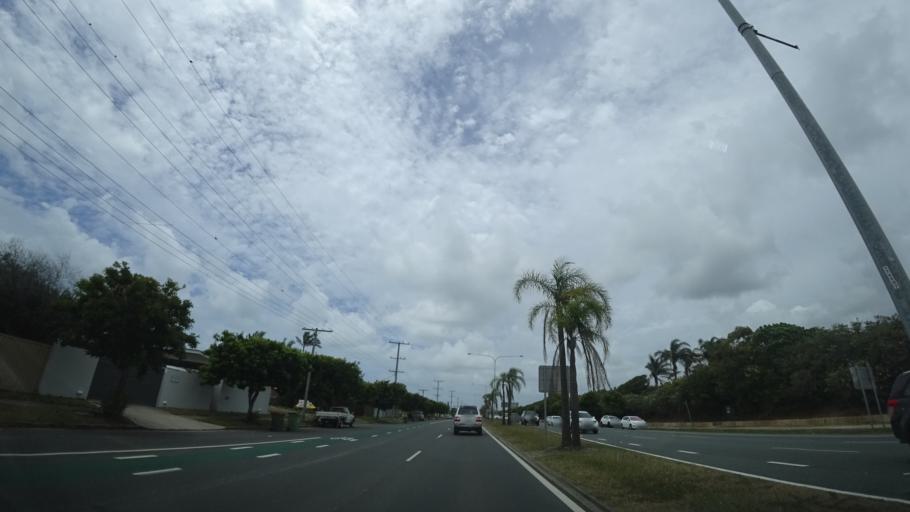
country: AU
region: Queensland
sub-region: Sunshine Coast
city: Mooloolaba
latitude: -26.7154
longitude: 153.1300
